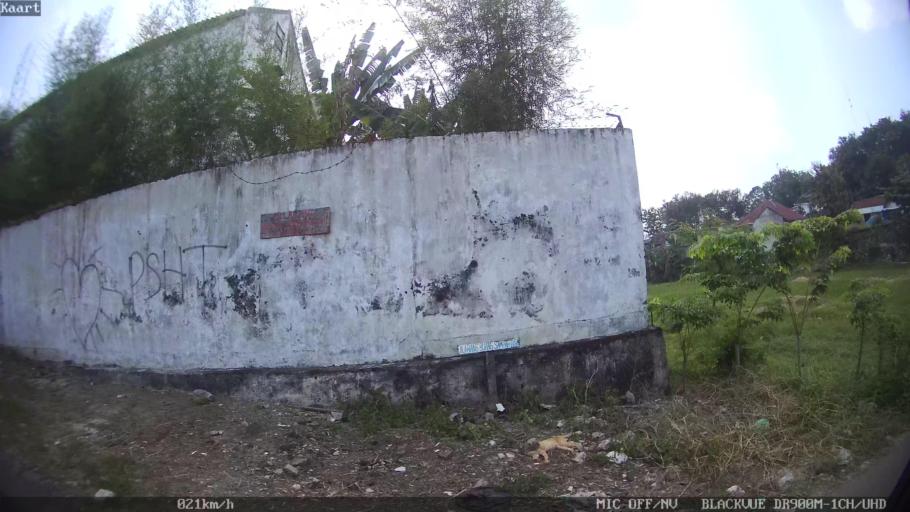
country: ID
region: Lampung
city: Pringsewu
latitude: -5.3576
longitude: 104.9628
